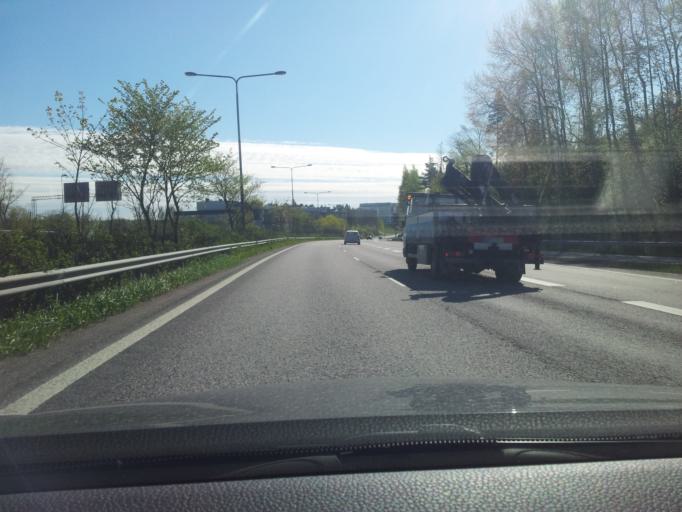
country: FI
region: Uusimaa
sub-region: Helsinki
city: Teekkarikylae
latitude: 60.2093
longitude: 24.8200
